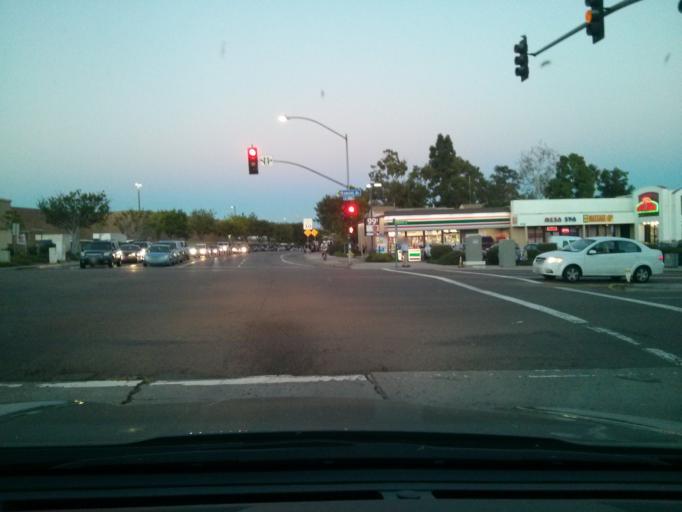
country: US
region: California
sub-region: San Diego County
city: La Jolla
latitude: 32.8171
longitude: -117.1811
